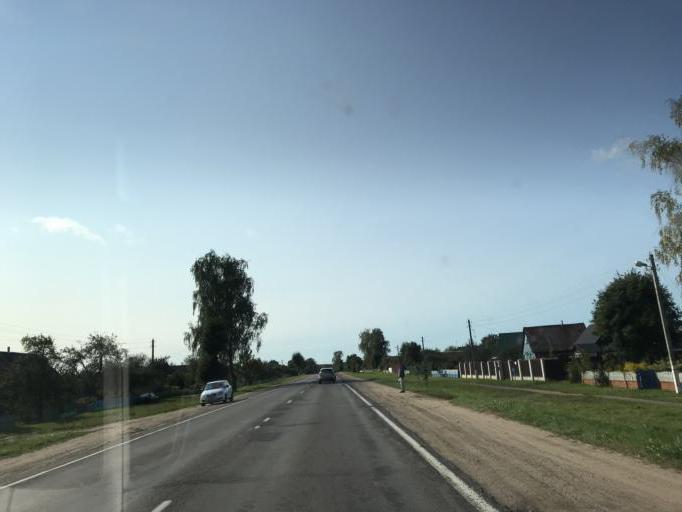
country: BY
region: Mogilev
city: Buynichy
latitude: 53.8382
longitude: 30.2473
